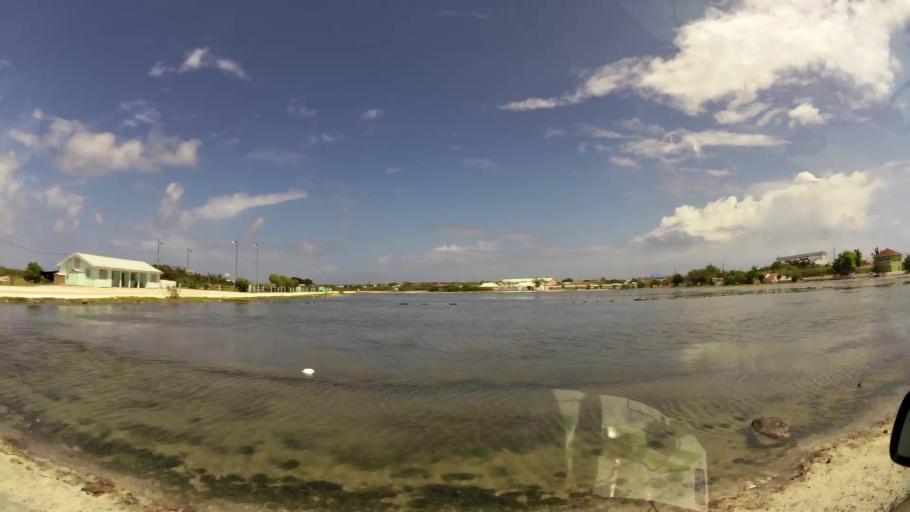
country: TC
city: Cockburn Town
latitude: 21.4781
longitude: -71.1468
